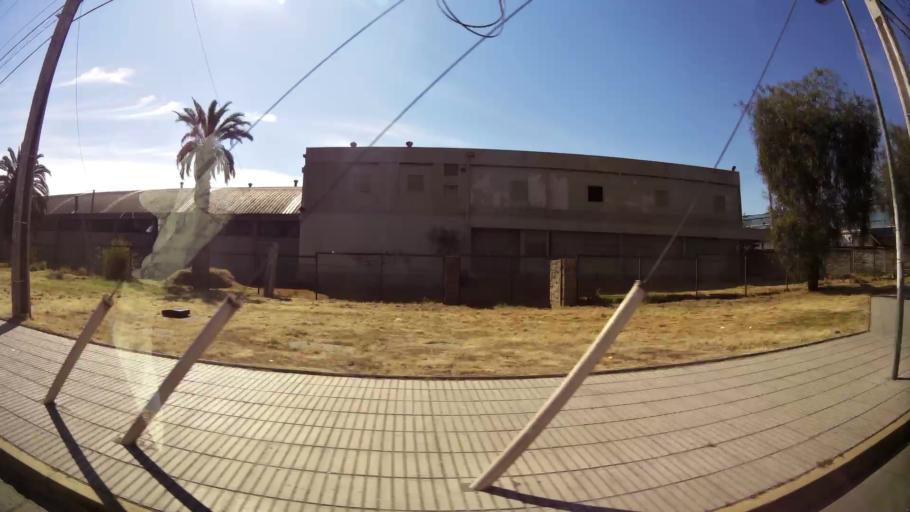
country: CL
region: Santiago Metropolitan
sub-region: Provincia de Santiago
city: Lo Prado
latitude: -33.5088
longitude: -70.7204
